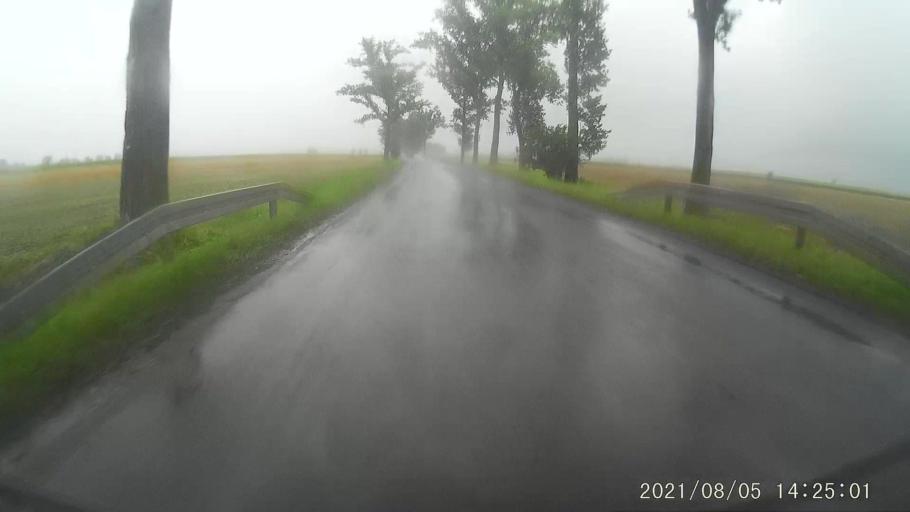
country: PL
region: Opole Voivodeship
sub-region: Powiat nyski
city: Korfantow
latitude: 50.4827
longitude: 17.6236
